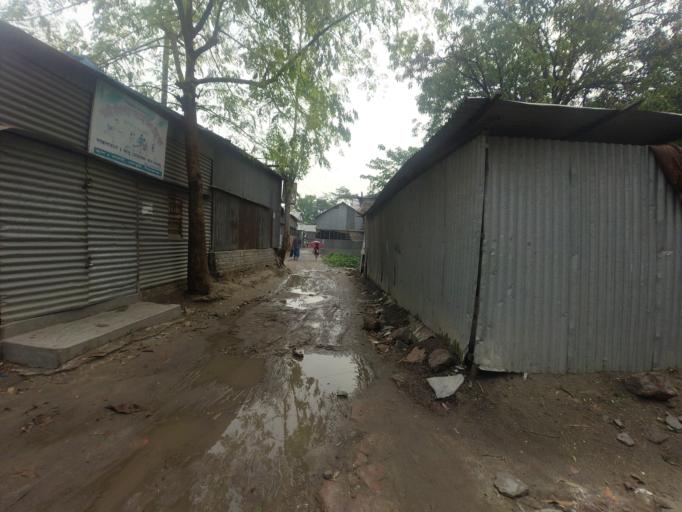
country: BD
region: Rajshahi
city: Sirajganj
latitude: 24.3262
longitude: 89.6886
